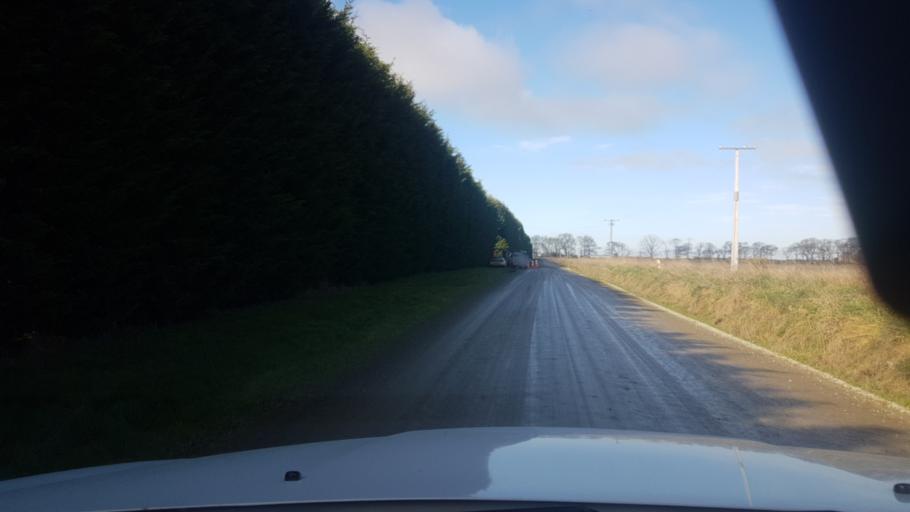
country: NZ
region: Canterbury
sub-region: Timaru District
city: Timaru
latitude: -44.3286
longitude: 171.2474
